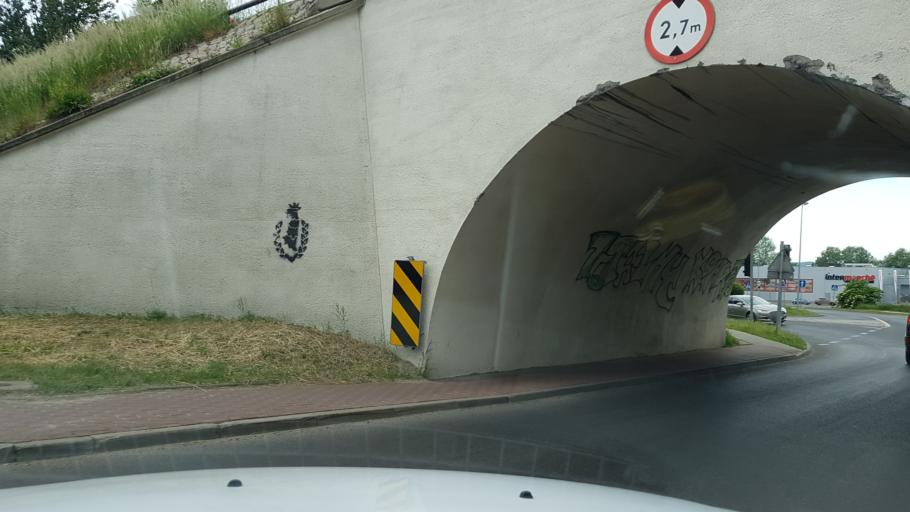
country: PL
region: West Pomeranian Voivodeship
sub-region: Powiat gryfinski
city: Gryfino
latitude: 53.2631
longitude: 14.4944
